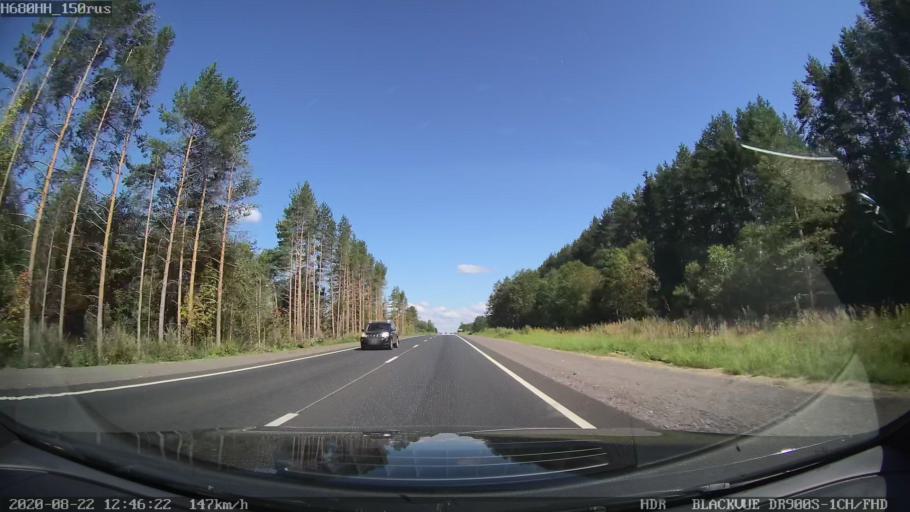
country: RU
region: Tverskaya
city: Rameshki
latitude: 57.4188
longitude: 36.1444
